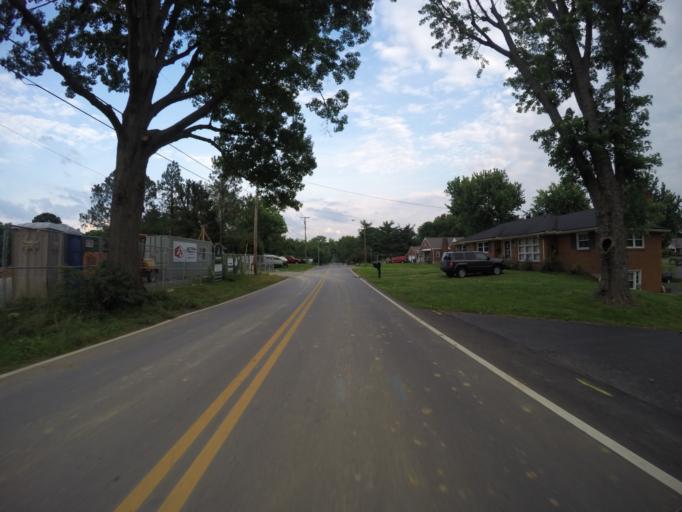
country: US
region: Tennessee
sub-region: Davidson County
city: Lakewood
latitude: 36.2494
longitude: -86.6381
